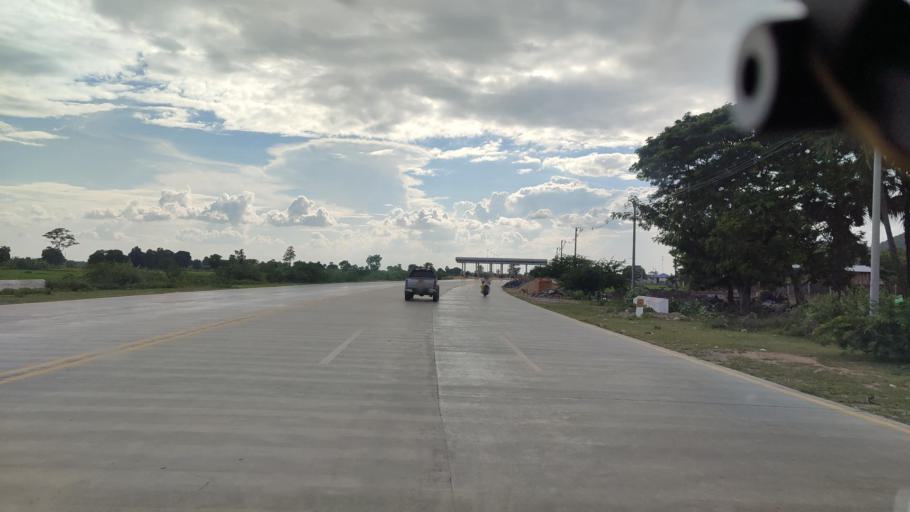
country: MM
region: Mandalay
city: Kyaukse
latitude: 21.6008
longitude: 96.1815
